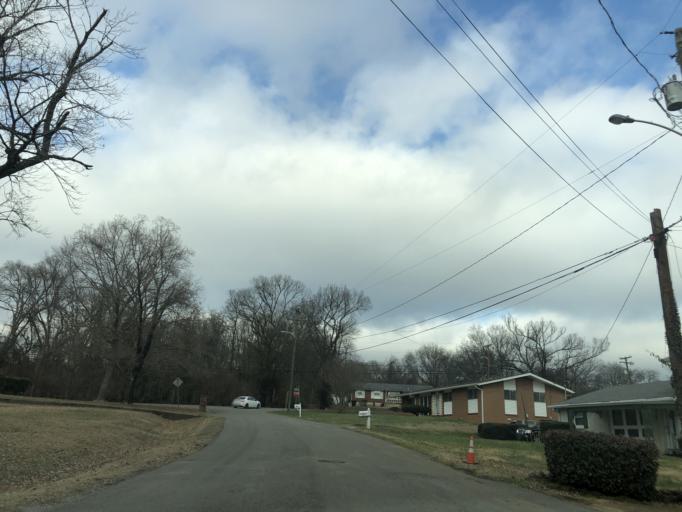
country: US
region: Tennessee
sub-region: Davidson County
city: Nashville
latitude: 36.2041
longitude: -86.8014
